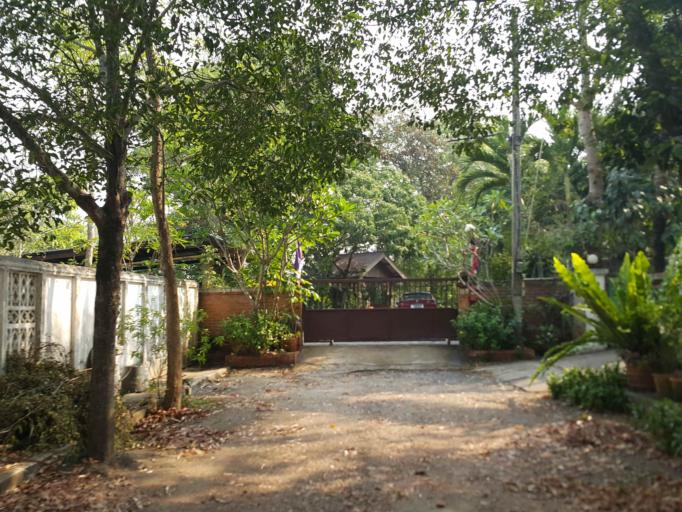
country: TH
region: Chiang Mai
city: Saraphi
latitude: 18.7676
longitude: 99.0621
